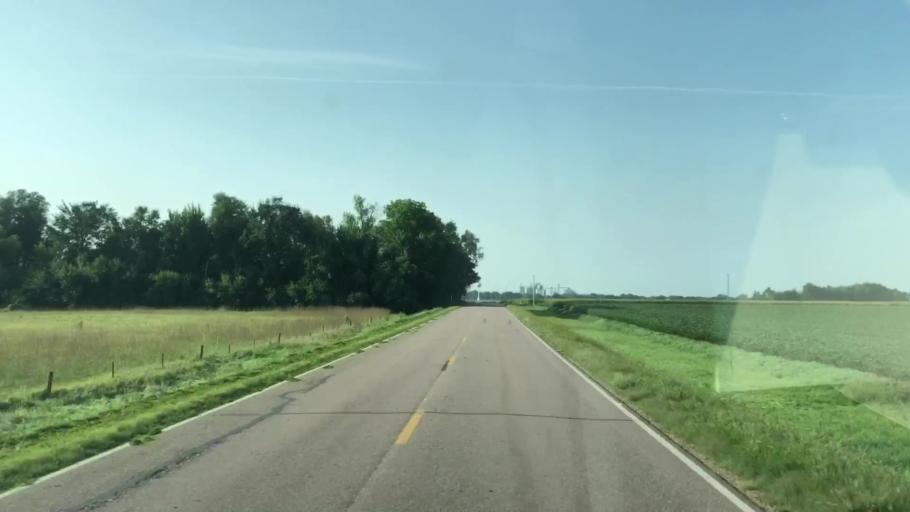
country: US
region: Iowa
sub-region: Lyon County
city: George
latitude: 43.2105
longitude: -96.0006
